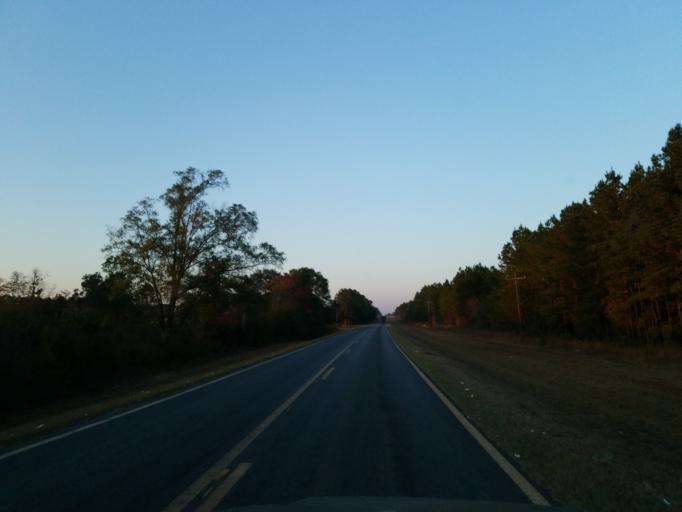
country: US
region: Georgia
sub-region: Ben Hill County
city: Fitzgerald
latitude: 31.6970
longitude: -83.3852
